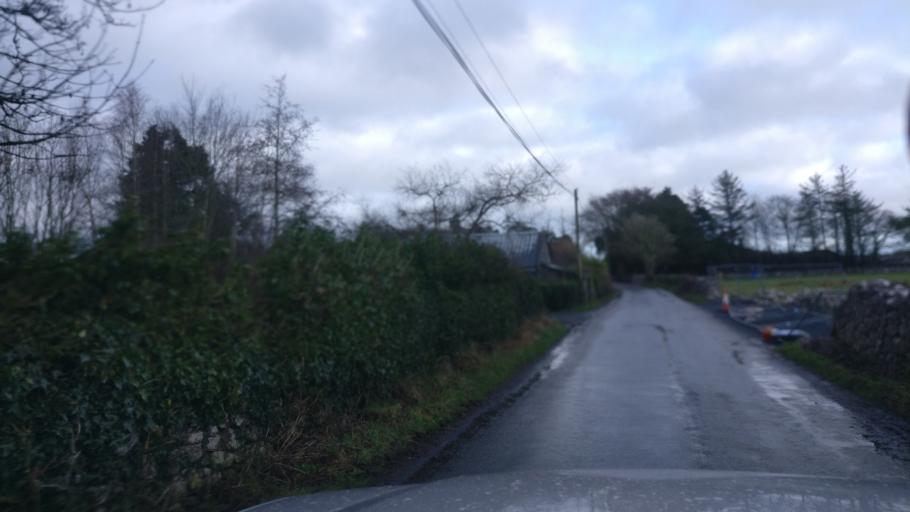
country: IE
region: Connaught
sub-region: County Galway
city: Loughrea
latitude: 53.2565
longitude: -8.6431
